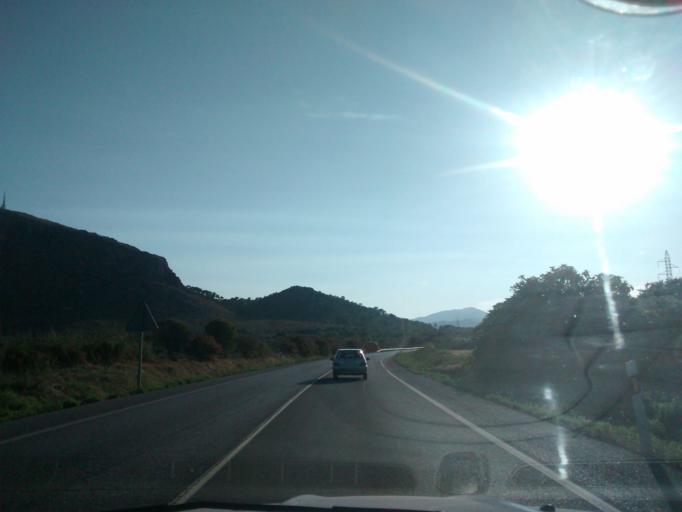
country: ES
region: Balearic Islands
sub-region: Illes Balears
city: Alcudia
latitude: 39.8420
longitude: 3.1066
